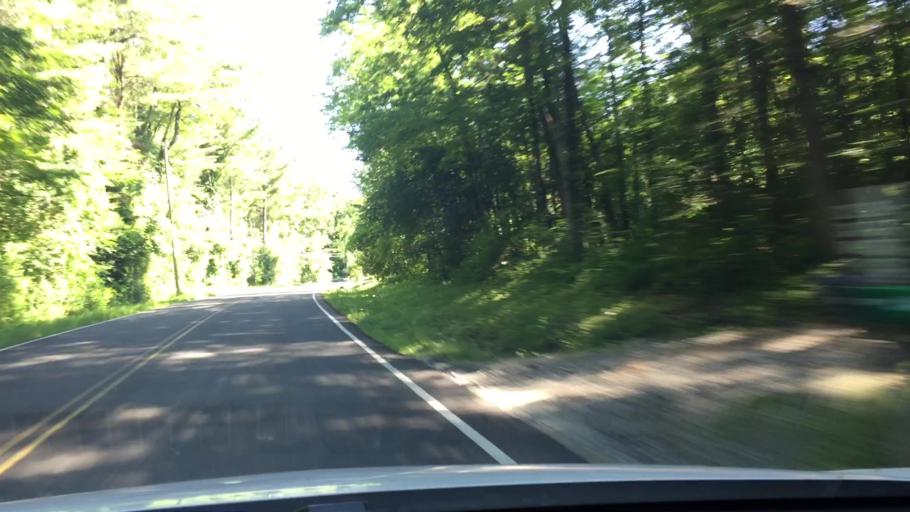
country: US
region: Massachusetts
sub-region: Berkshire County
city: West Stockbridge
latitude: 42.3595
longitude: -73.3538
